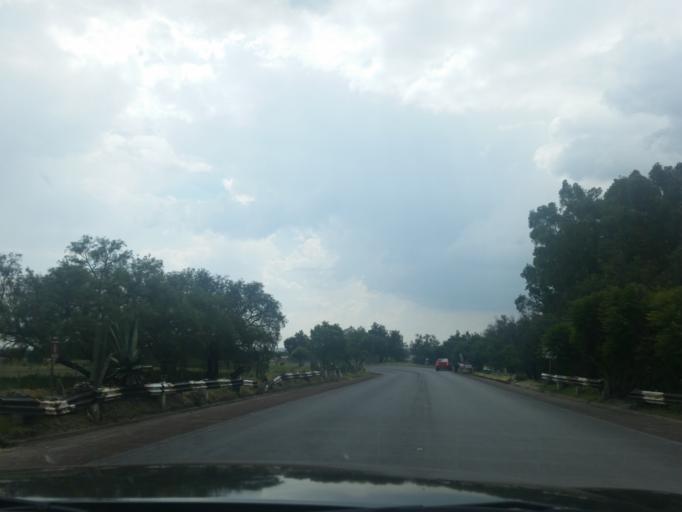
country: MX
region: Mexico
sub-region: Teotihuacan
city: Teotihuacan de Arista
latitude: 19.6840
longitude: -98.8535
